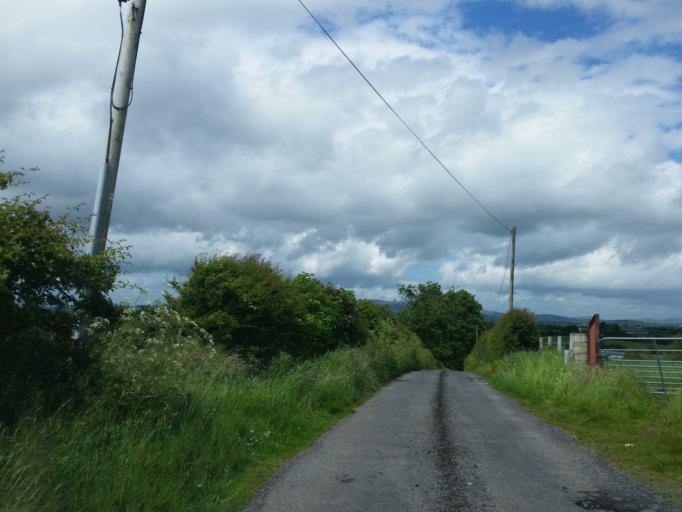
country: GB
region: Northern Ireland
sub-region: Omagh District
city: Omagh
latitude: 54.5451
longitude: -7.1364
